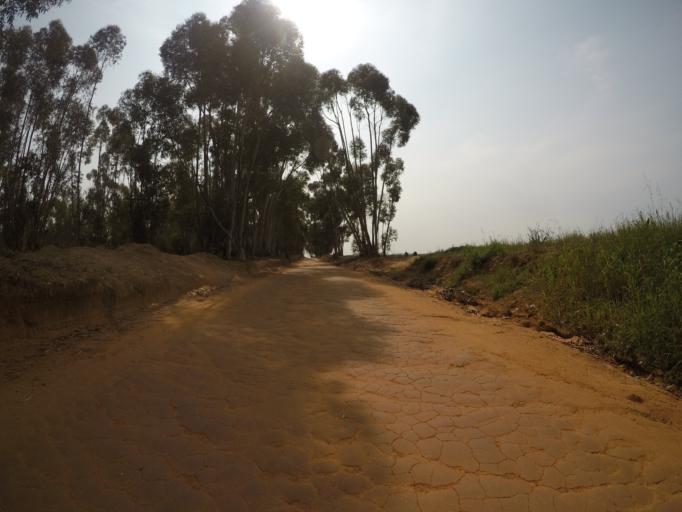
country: ZA
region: Western Cape
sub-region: West Coast District Municipality
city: Malmesbury
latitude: -33.4576
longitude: 18.7401
